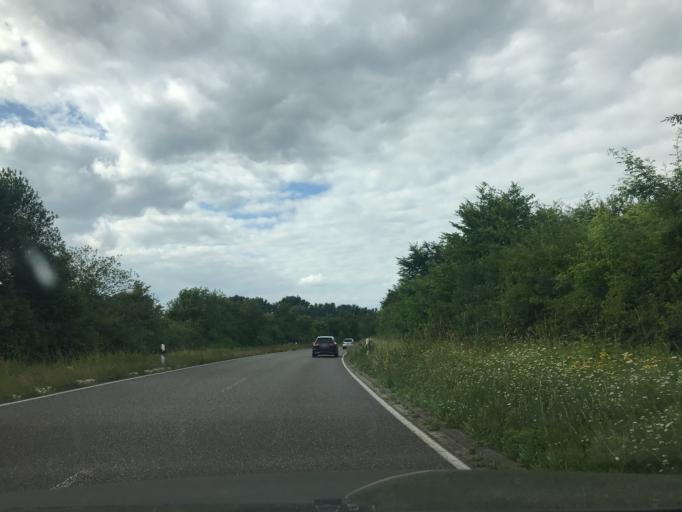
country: DE
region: North Rhine-Westphalia
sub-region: Regierungsbezirk Dusseldorf
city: Neuss
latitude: 51.1535
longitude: 6.7166
